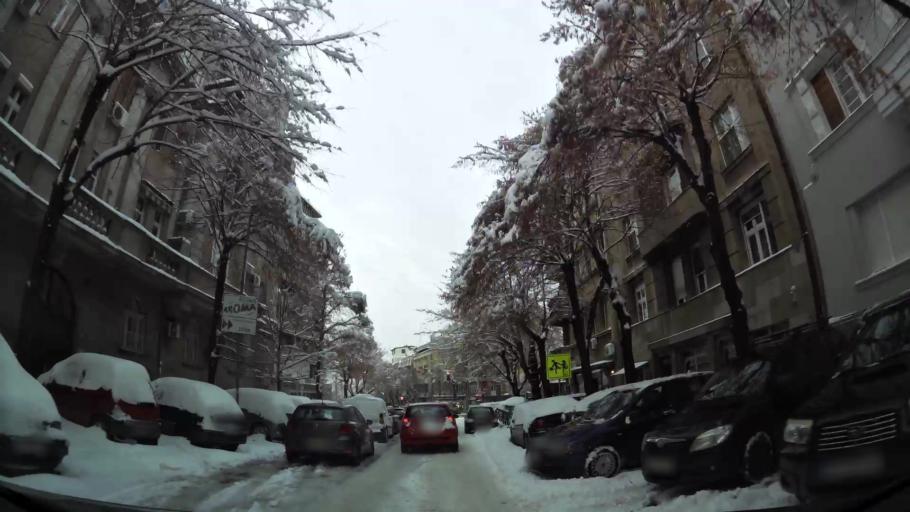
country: RS
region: Central Serbia
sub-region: Belgrade
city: Stari Grad
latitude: 44.8148
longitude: 20.4701
